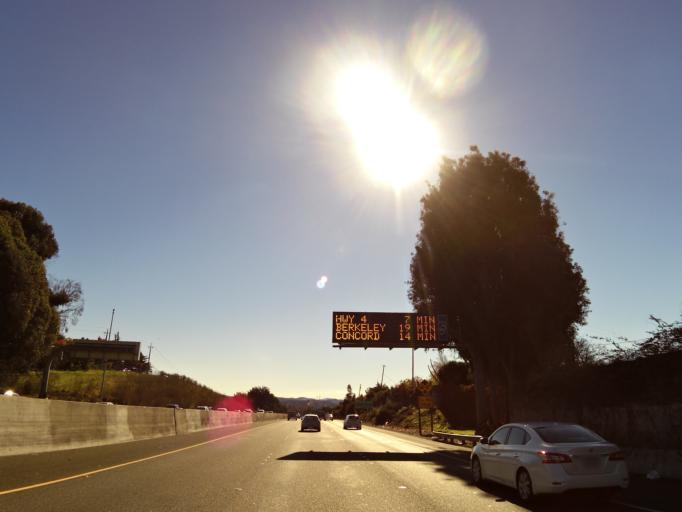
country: US
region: California
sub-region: Solano County
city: Vallejo
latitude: 38.1177
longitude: -122.2304
